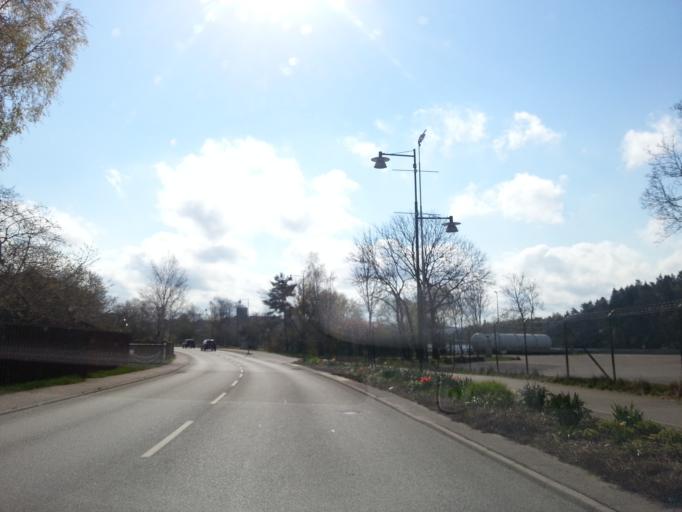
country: SE
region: Vaestra Goetaland
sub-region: Kungalvs Kommun
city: Kungalv
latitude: 57.8669
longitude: 11.9862
